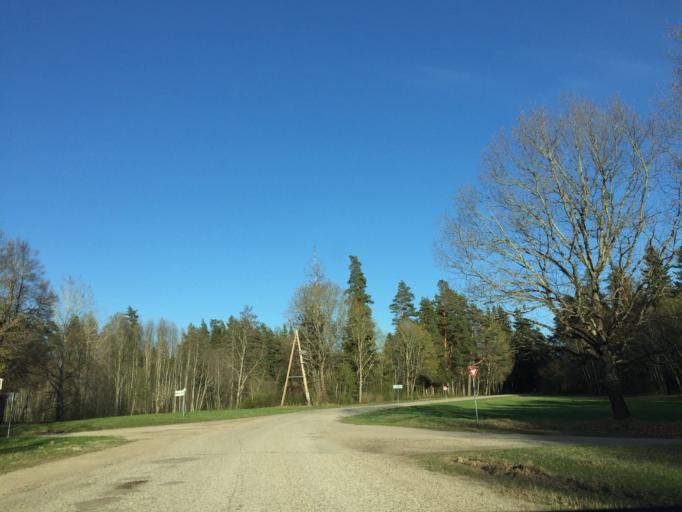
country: LV
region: Valkas Rajons
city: Valka
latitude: 57.7932
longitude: 25.9768
